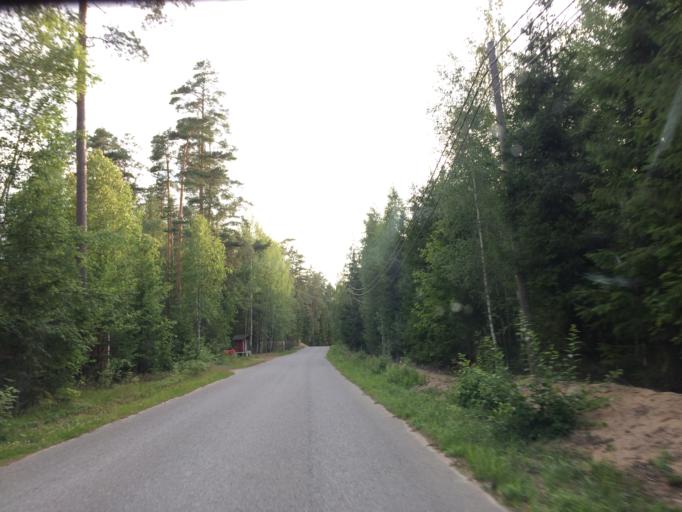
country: FI
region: Haeme
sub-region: Haemeenlinna
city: Tervakoski
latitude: 60.8547
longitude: 24.6143
